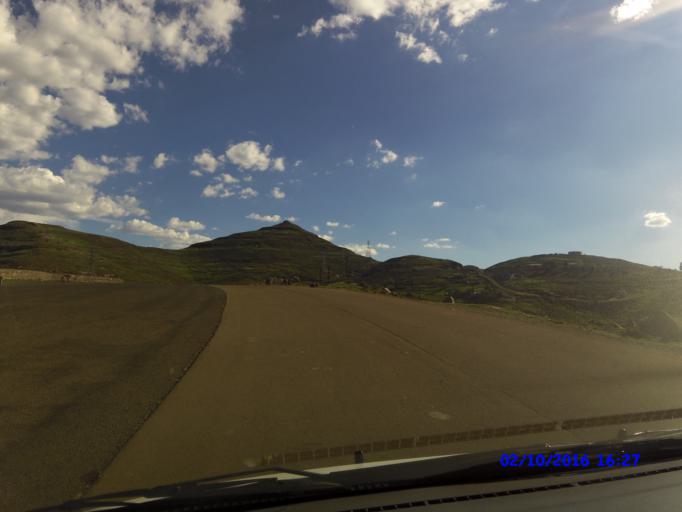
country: LS
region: Maseru
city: Nako
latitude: -29.4695
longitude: 28.0897
